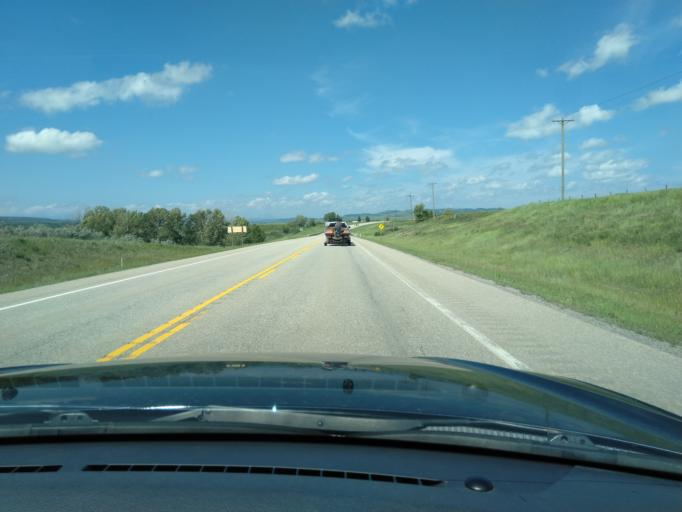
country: CA
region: Alberta
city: Cochrane
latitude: 51.2074
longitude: -114.5164
